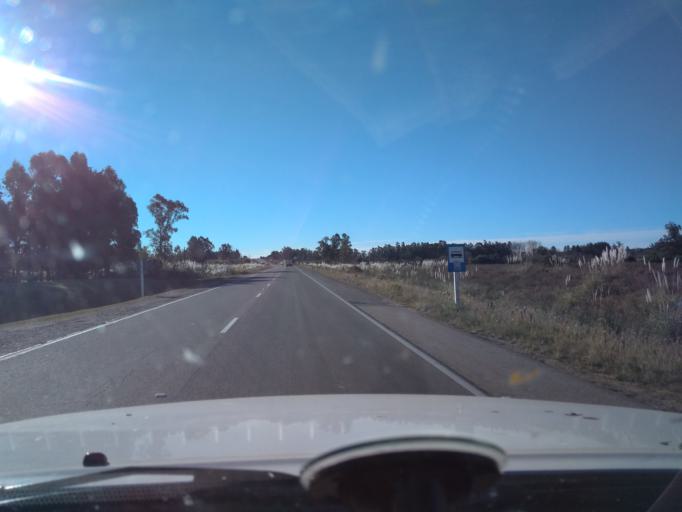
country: UY
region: Canelones
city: Sauce
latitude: -34.5977
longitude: -56.0508
